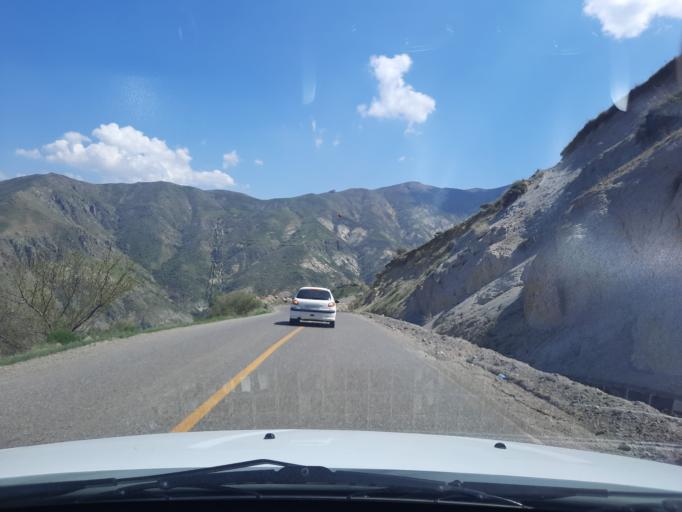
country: IR
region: Qazvin
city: Qazvin
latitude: 36.4118
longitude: 50.2435
